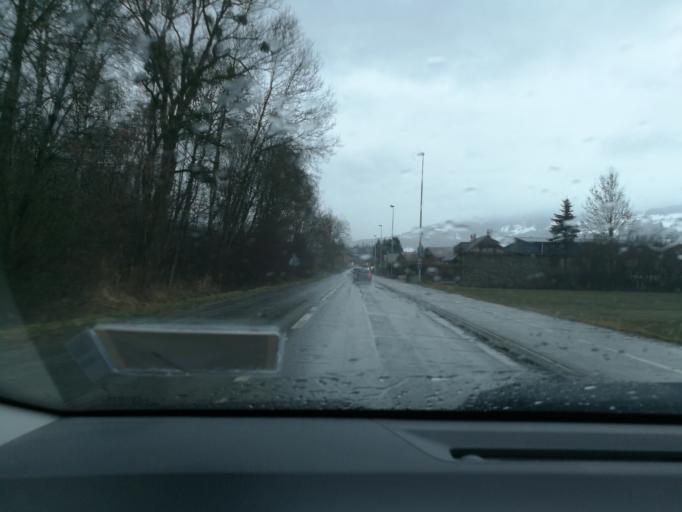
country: FR
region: Rhone-Alpes
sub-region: Departement de la Haute-Savoie
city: Domancy
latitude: 45.9342
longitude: 6.6496
